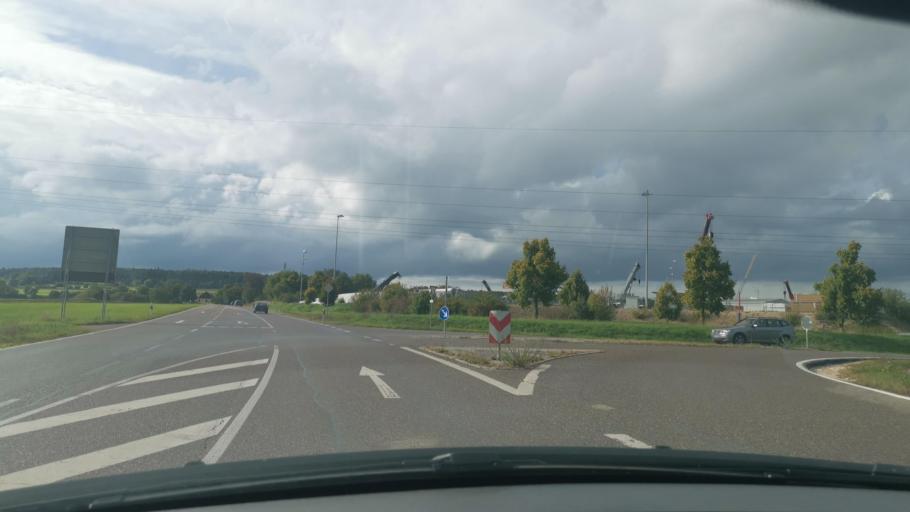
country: DE
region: Baden-Wuerttemberg
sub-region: Tuebingen Region
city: Ehingen
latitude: 48.2970
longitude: 9.7015
